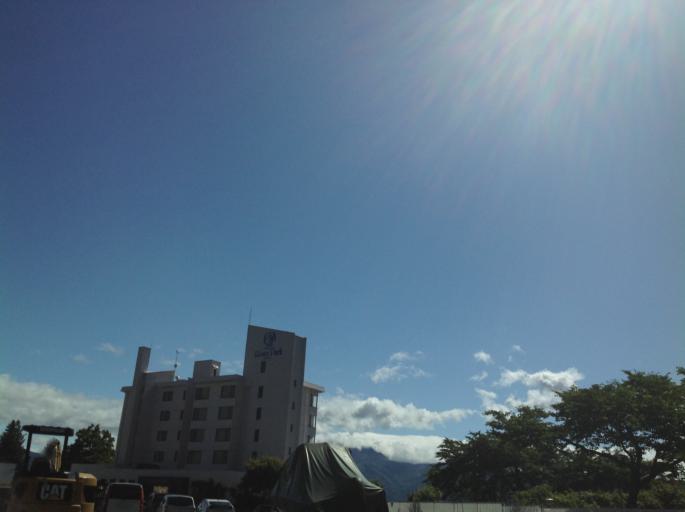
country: JP
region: Akita
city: Kakunodatemachi
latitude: 39.7123
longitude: 140.6337
